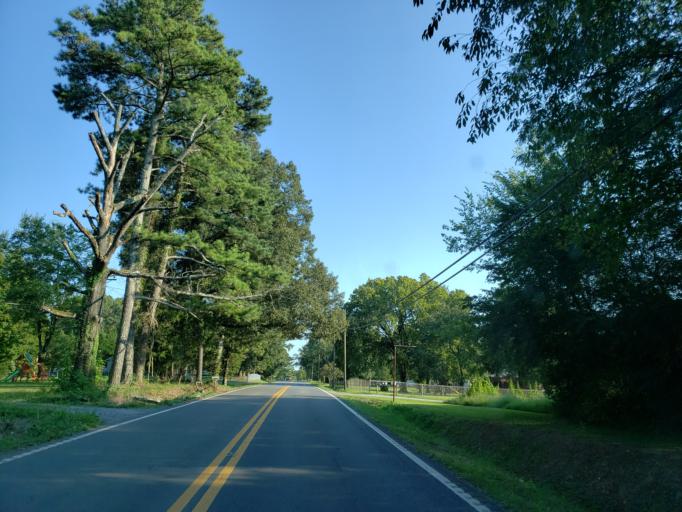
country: US
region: Tennessee
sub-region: Bradley County
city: Wildwood Lake
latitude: 35.0422
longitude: -84.8054
